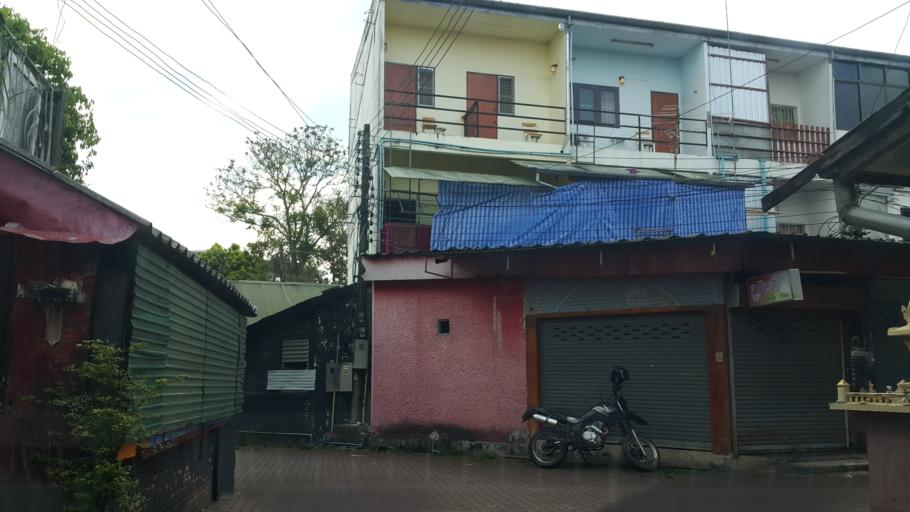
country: TH
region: Chiang Rai
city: Chiang Rai
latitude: 19.9064
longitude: 99.8314
